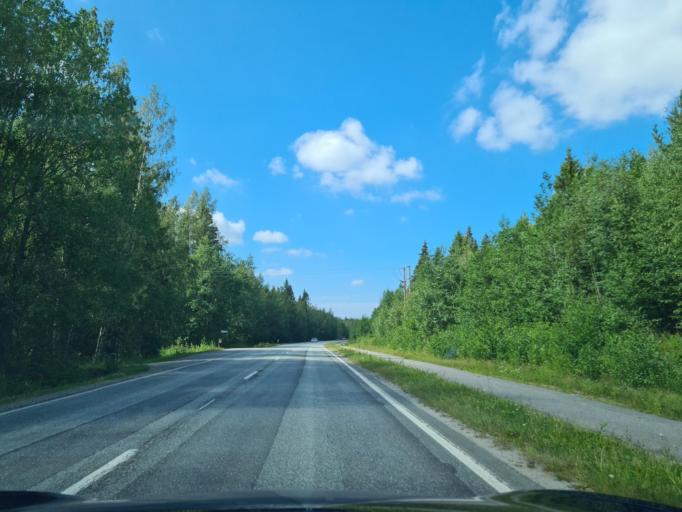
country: FI
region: Ostrobothnia
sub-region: Vaasa
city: Replot
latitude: 63.1988
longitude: 21.5379
